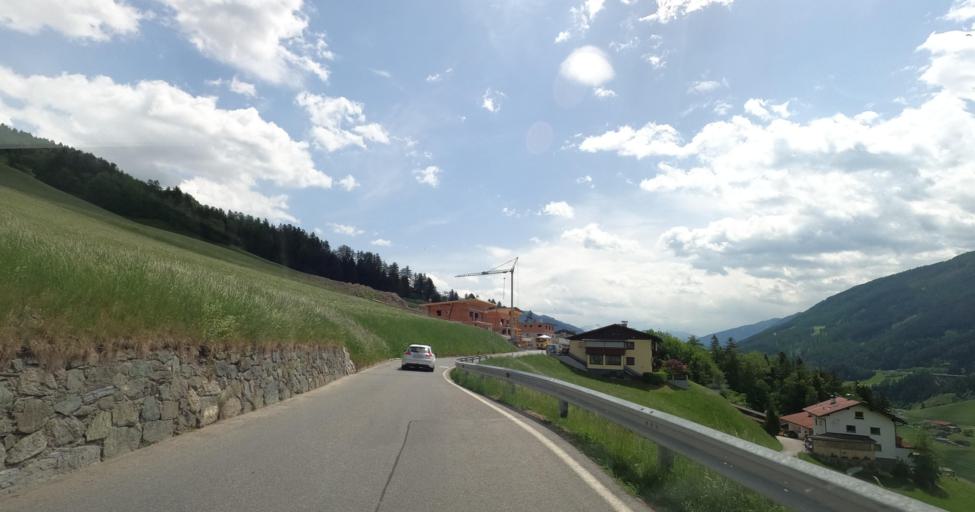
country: AT
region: Tyrol
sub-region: Politischer Bezirk Innsbruck Land
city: Ellbogen
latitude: 47.1755
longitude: 11.4397
